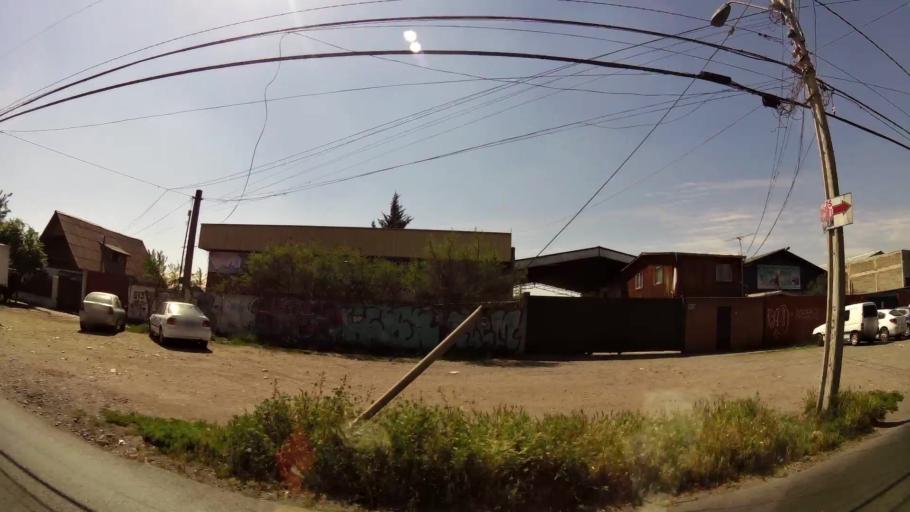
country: CL
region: Santiago Metropolitan
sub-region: Provincia de Santiago
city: Santiago
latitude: -33.5182
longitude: -70.6405
